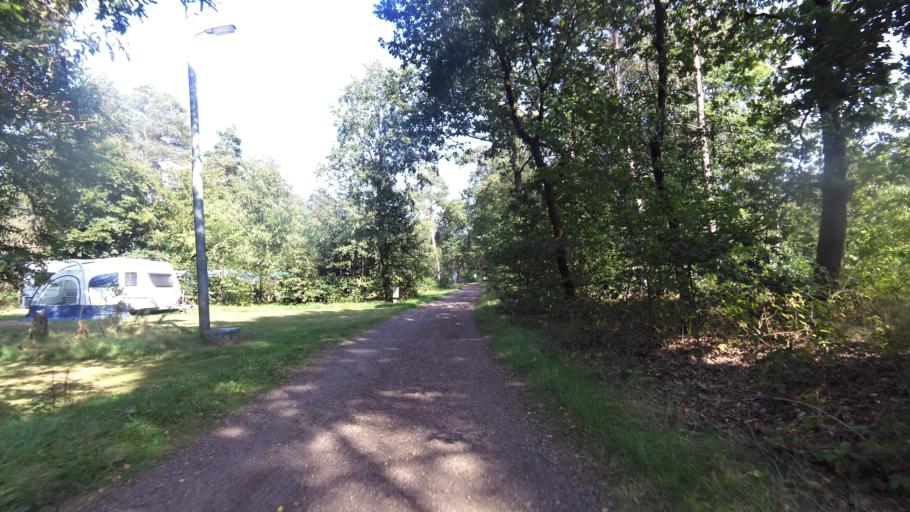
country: NL
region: Gelderland
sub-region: Gemeente Ede
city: Harskamp
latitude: 52.1513
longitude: 5.7454
